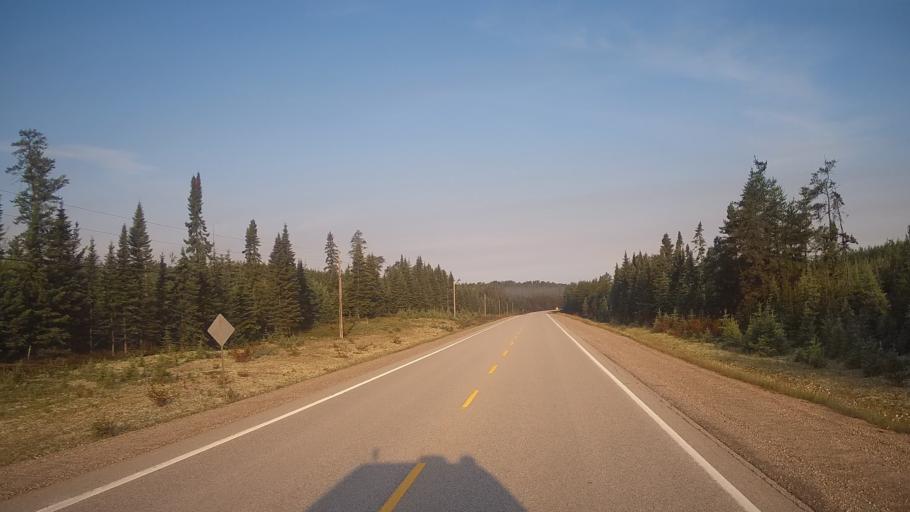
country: CA
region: Ontario
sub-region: Rainy River District
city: Atikokan
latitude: 49.2589
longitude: -91.1797
